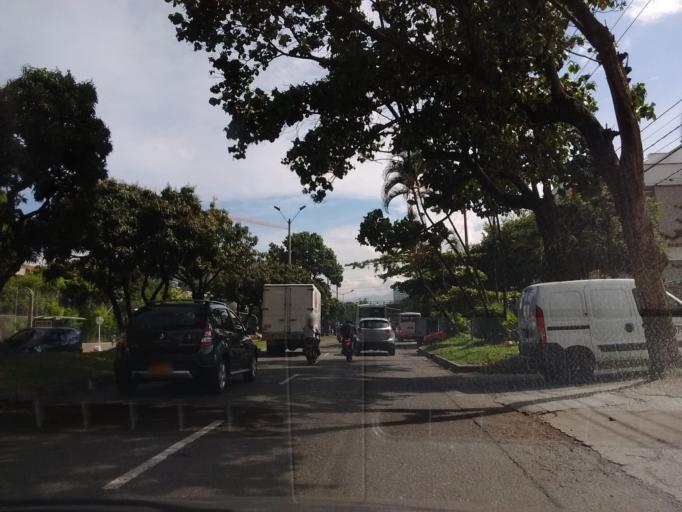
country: CO
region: Antioquia
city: Itagui
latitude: 6.2117
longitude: -75.5763
